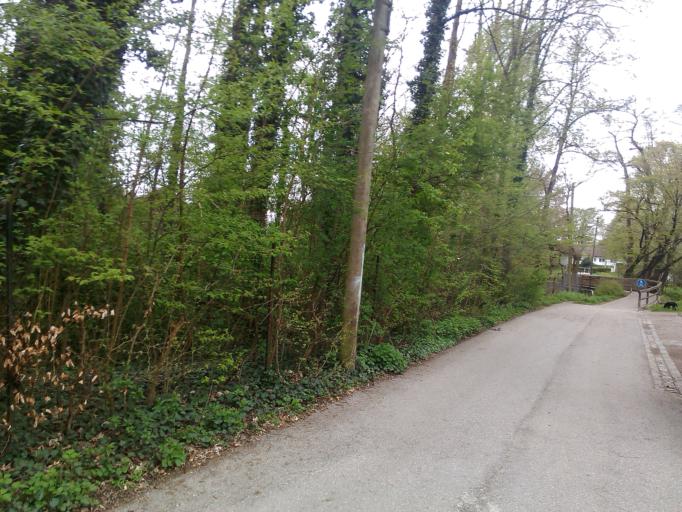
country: DE
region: Bavaria
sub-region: Upper Bavaria
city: Krailling
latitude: 48.0889
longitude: 11.4015
